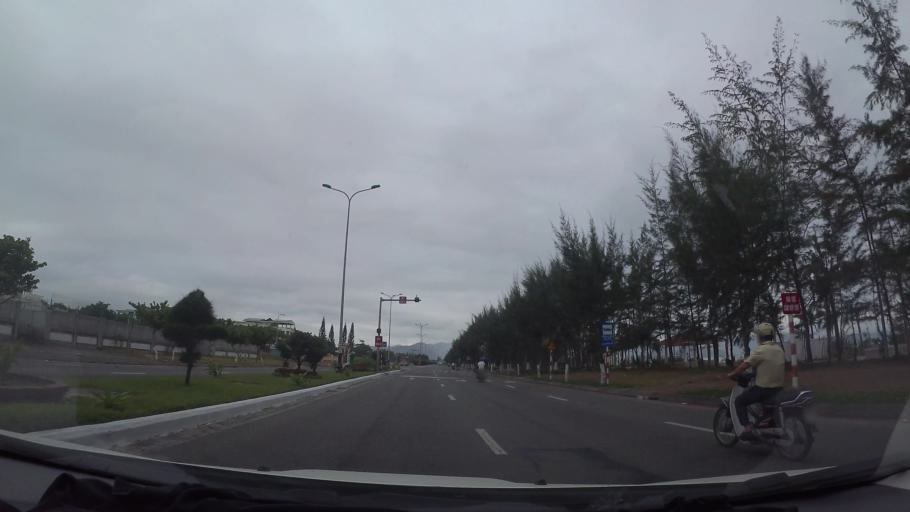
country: VN
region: Da Nang
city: Lien Chieu
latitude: 16.0916
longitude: 108.1503
